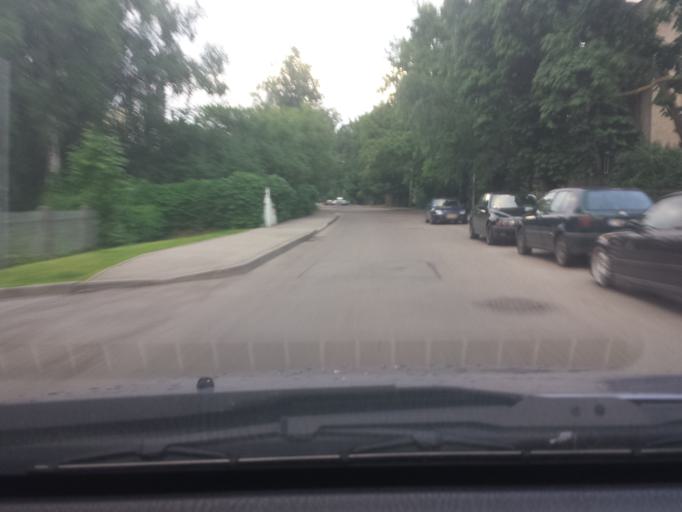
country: LV
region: Riga
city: Jaunciems
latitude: 56.9701
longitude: 24.1707
